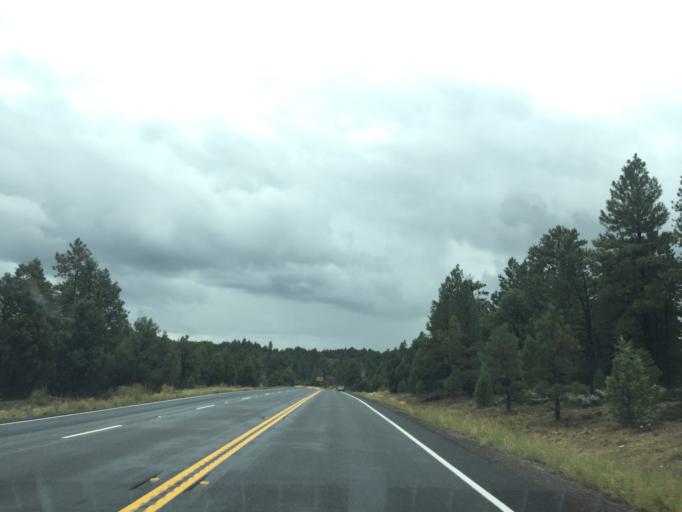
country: US
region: Utah
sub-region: Garfield County
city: Panguitch
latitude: 37.4776
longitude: -112.5137
